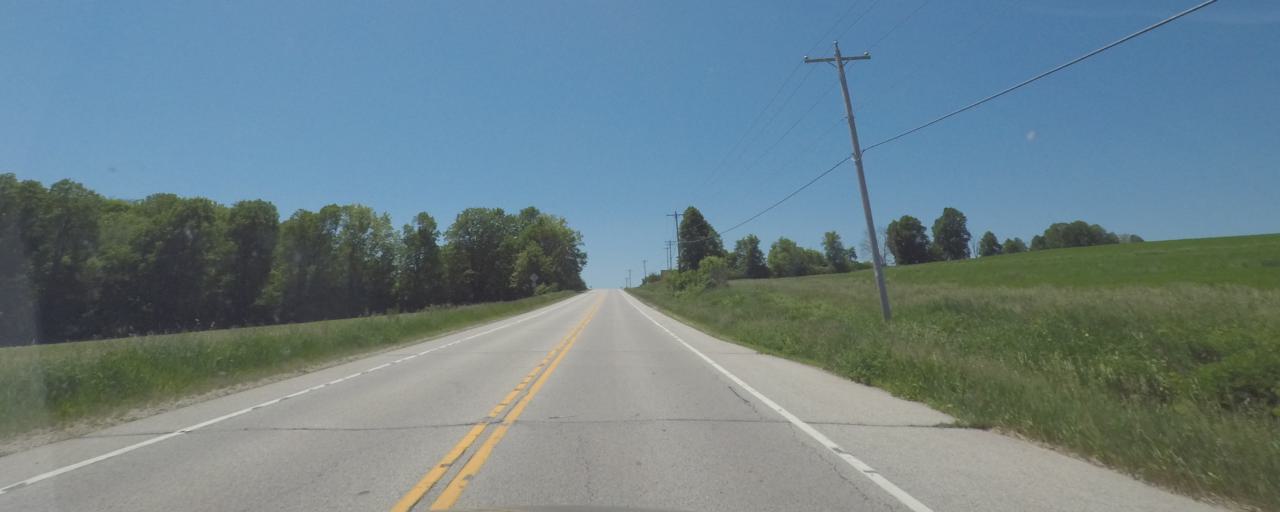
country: US
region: Wisconsin
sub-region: Ozaukee County
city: Kohler
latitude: 43.5836
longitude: -88.0525
